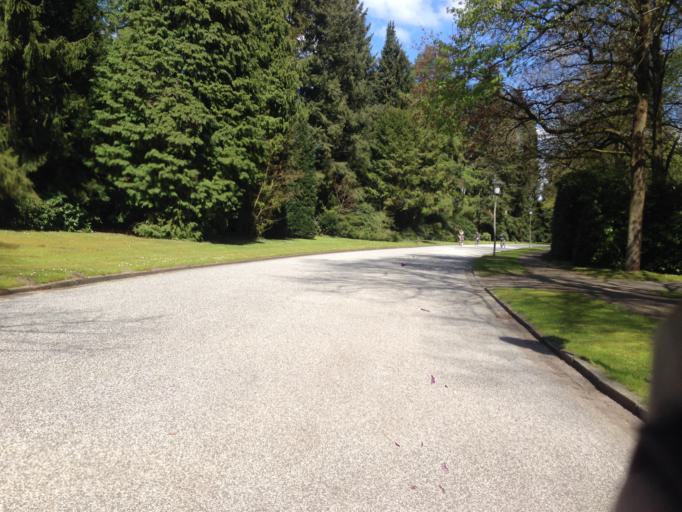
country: DE
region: Hamburg
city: Ohlsdorf
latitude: 53.6275
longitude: 10.0387
